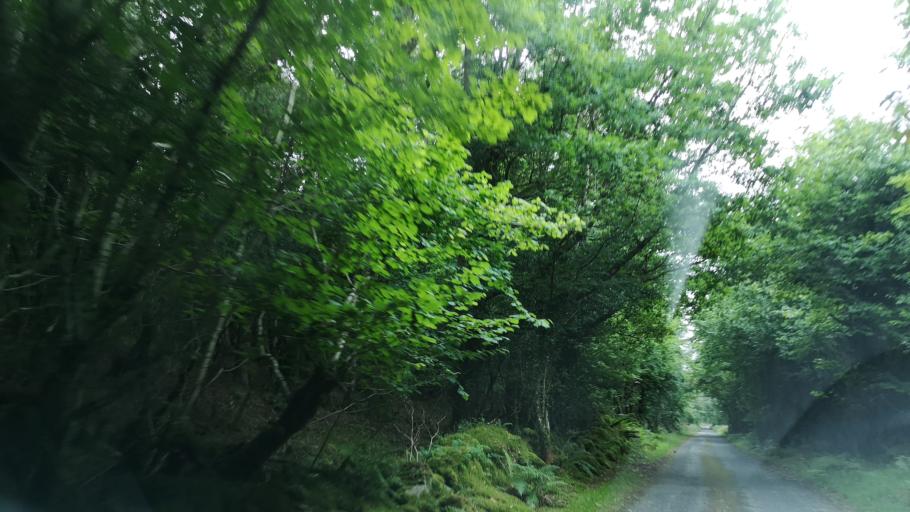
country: IE
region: Connaught
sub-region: County Galway
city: Loughrea
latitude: 53.1360
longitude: -8.4794
